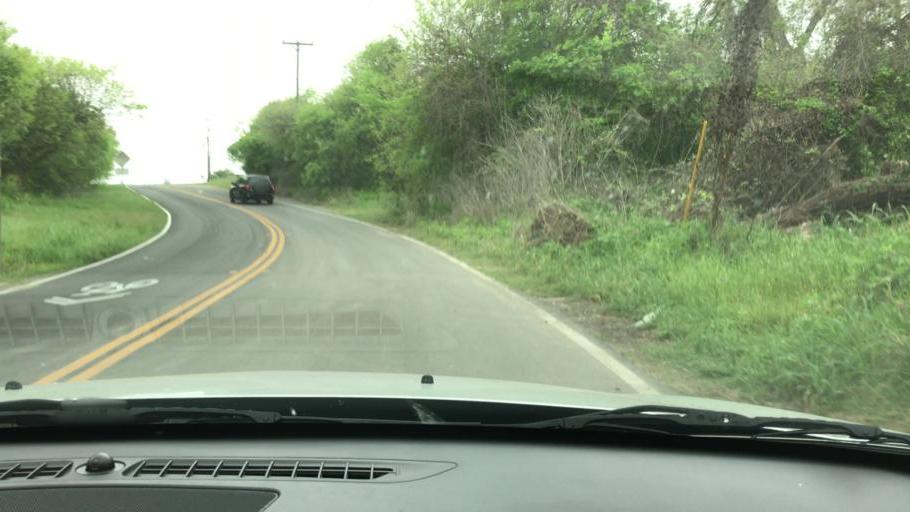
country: US
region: Texas
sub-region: Bexar County
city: San Antonio
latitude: 29.3353
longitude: -98.4584
